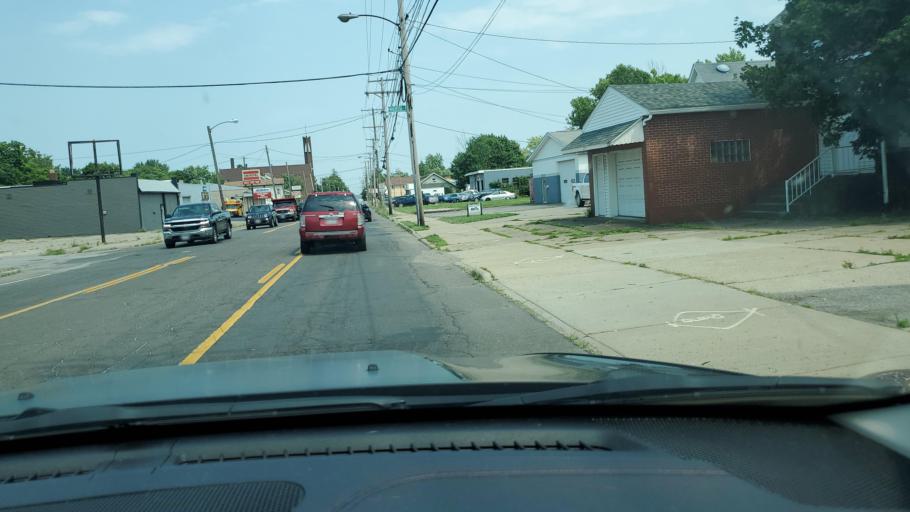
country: US
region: Ohio
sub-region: Mahoning County
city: Youngstown
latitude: 41.1029
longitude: -80.6970
